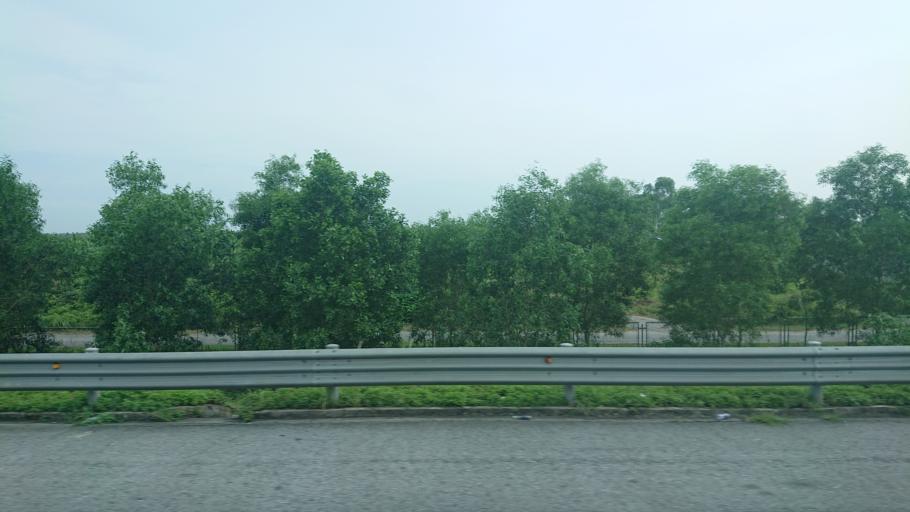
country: VN
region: Hai Duong
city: Tu Ky
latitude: 20.8230
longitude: 106.4705
